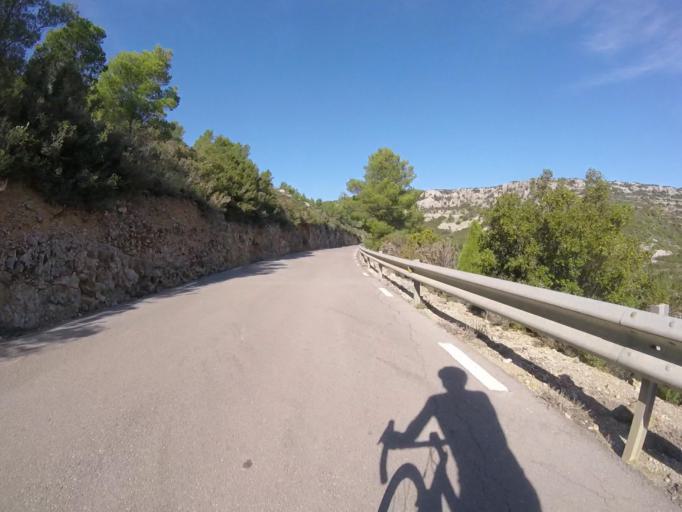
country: ES
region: Valencia
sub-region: Provincia de Castello
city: Sarratella
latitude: 40.2715
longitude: 0.0499
